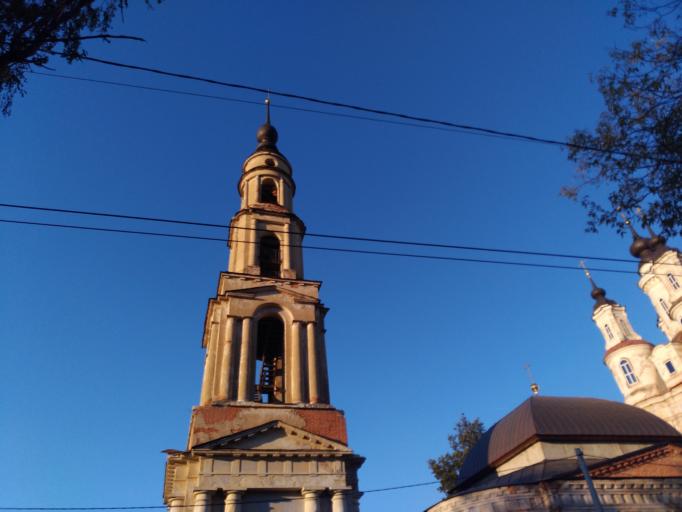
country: RU
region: Kaluga
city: Kaluga
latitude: 54.5146
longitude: 36.2734
